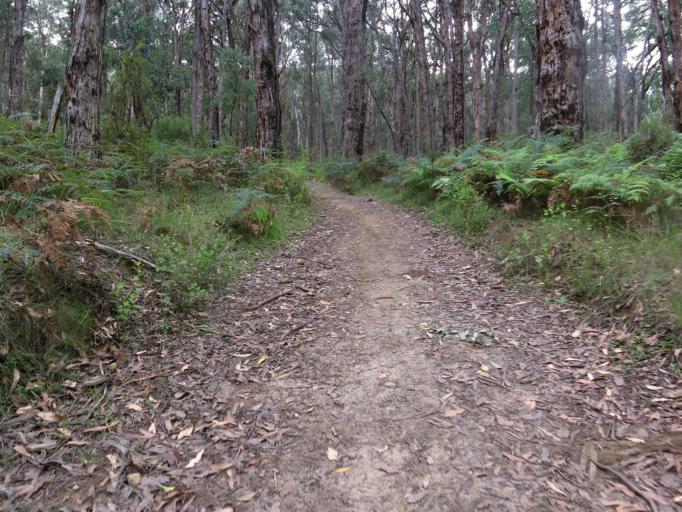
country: AU
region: Victoria
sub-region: Knox
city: The Basin
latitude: -37.8429
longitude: 145.3366
